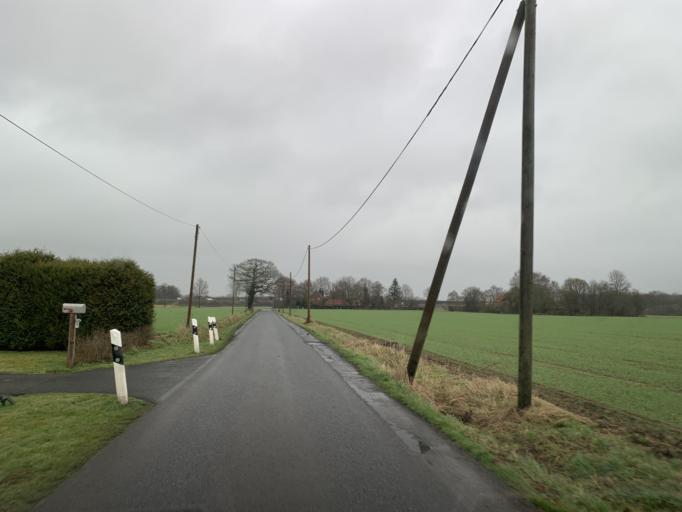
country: DE
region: North Rhine-Westphalia
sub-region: Regierungsbezirk Munster
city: Muenster
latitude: 51.9366
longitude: 7.5437
